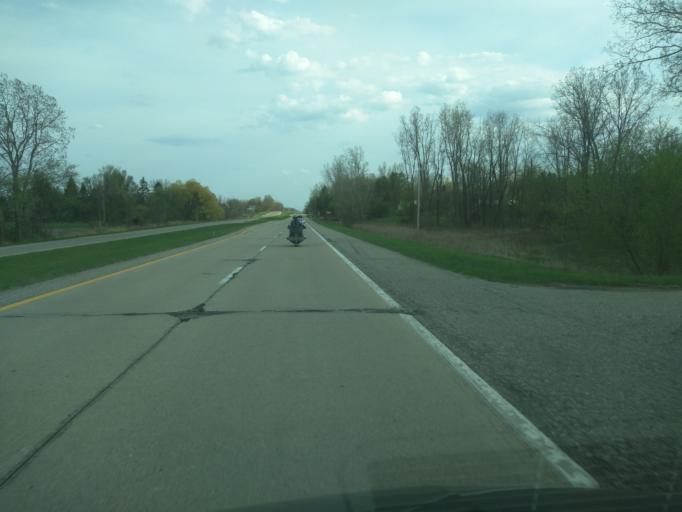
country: US
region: Michigan
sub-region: Eaton County
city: Dimondale
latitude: 42.6023
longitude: -84.6226
